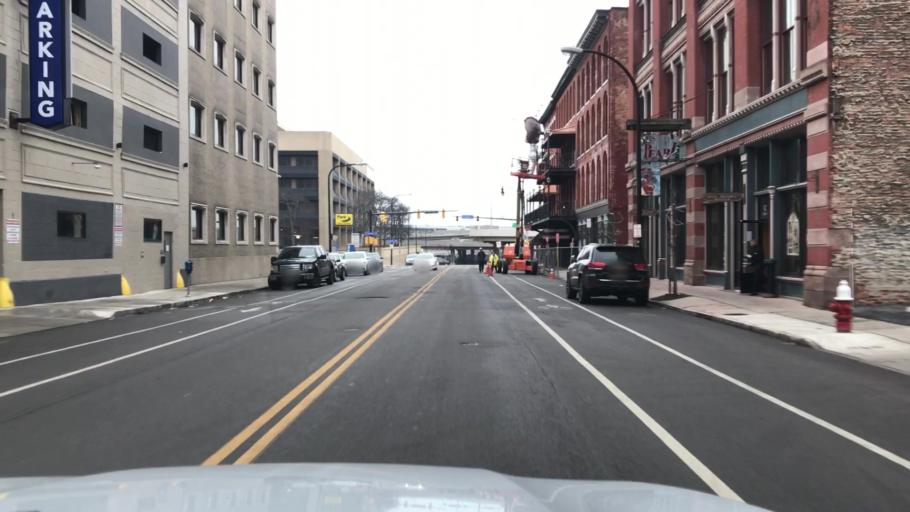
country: US
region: New York
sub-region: Erie County
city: Buffalo
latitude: 42.8817
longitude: -78.8769
